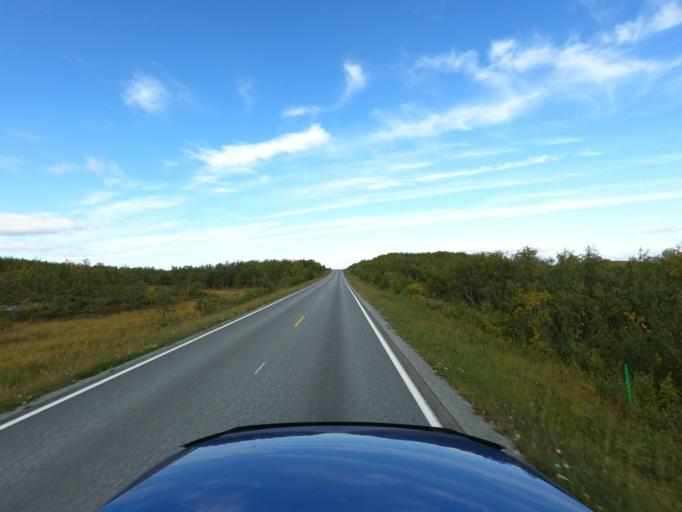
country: NO
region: Finnmark Fylke
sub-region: Karasjok
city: Karasjohka
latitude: 69.6921
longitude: 25.2591
